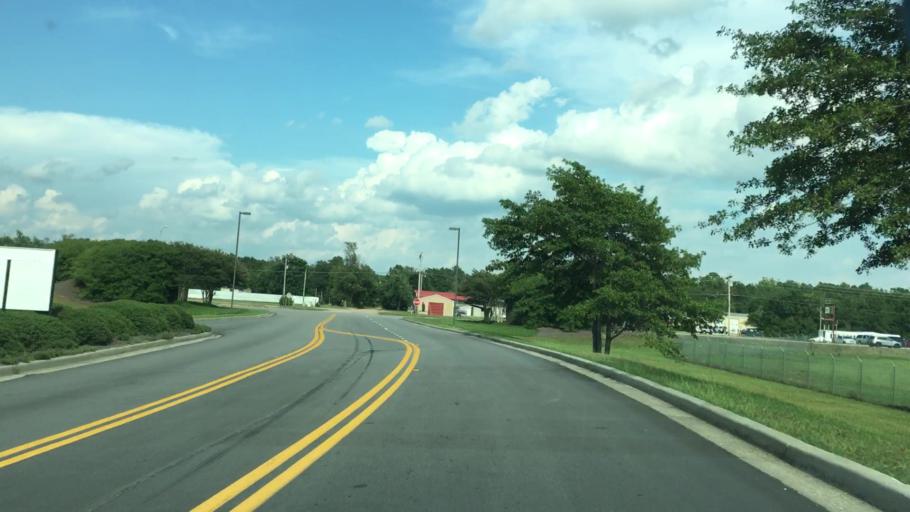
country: US
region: South Carolina
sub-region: Aiken County
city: Aiken
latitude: 33.6564
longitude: -81.6761
